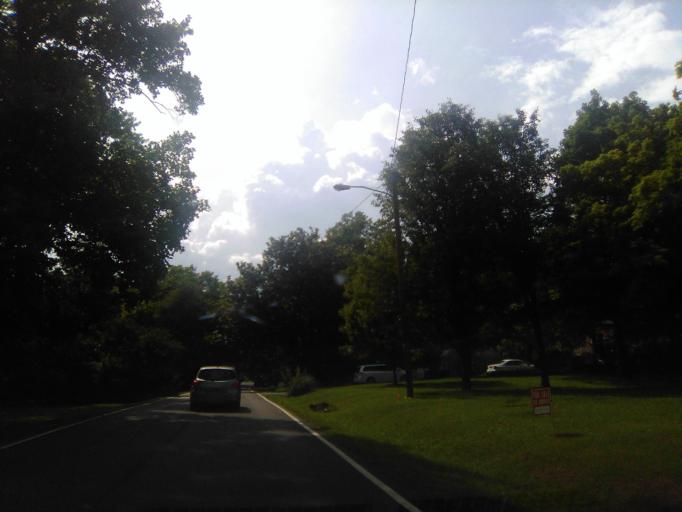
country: US
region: Tennessee
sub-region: Davidson County
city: Belle Meade
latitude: 36.0934
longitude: -86.8746
